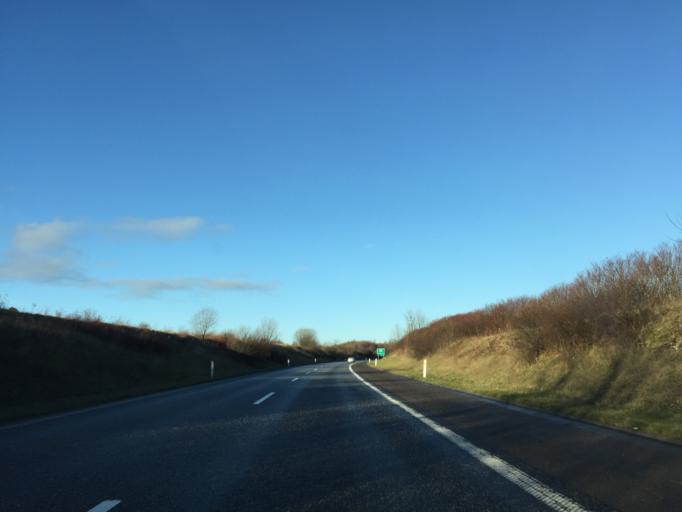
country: DK
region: South Denmark
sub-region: Fredericia Kommune
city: Taulov
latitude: 55.5980
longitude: 9.5898
